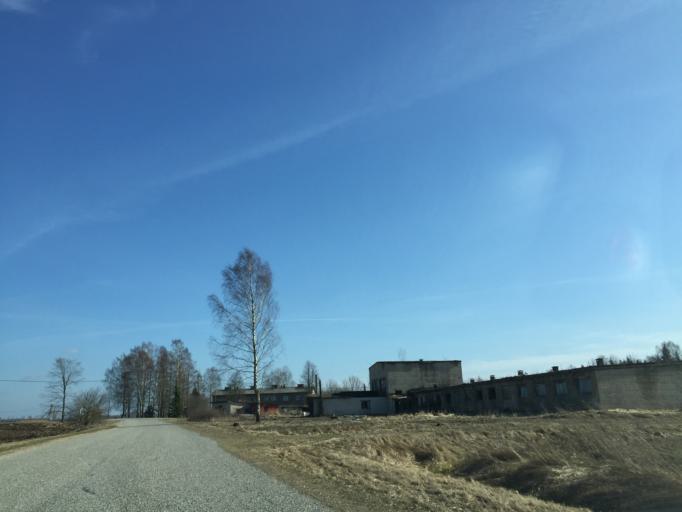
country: LV
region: Saulkrastu
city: Saulkrasti
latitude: 57.3492
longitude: 24.5556
